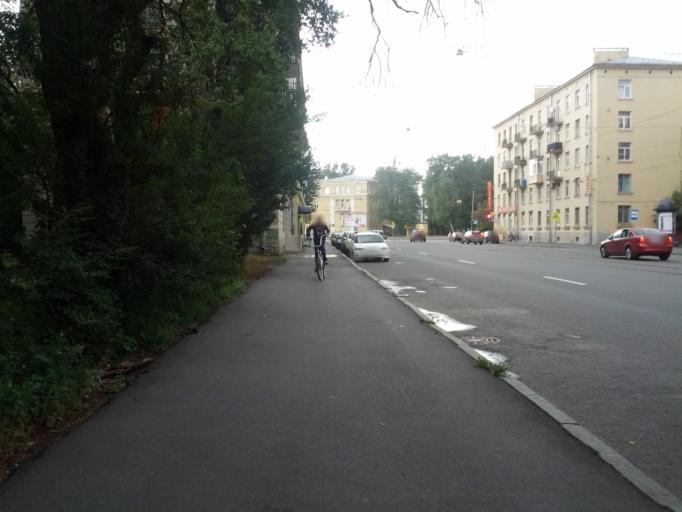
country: RU
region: St.-Petersburg
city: Centralniy
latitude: 59.9350
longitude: 30.4077
